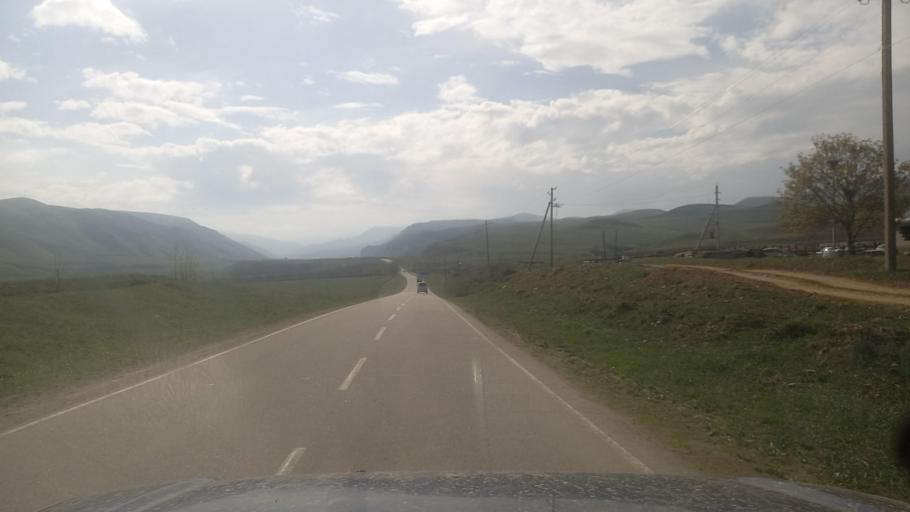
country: RU
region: Kabardino-Balkariya
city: Kamennomostskoye
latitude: 43.7360
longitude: 43.0040
